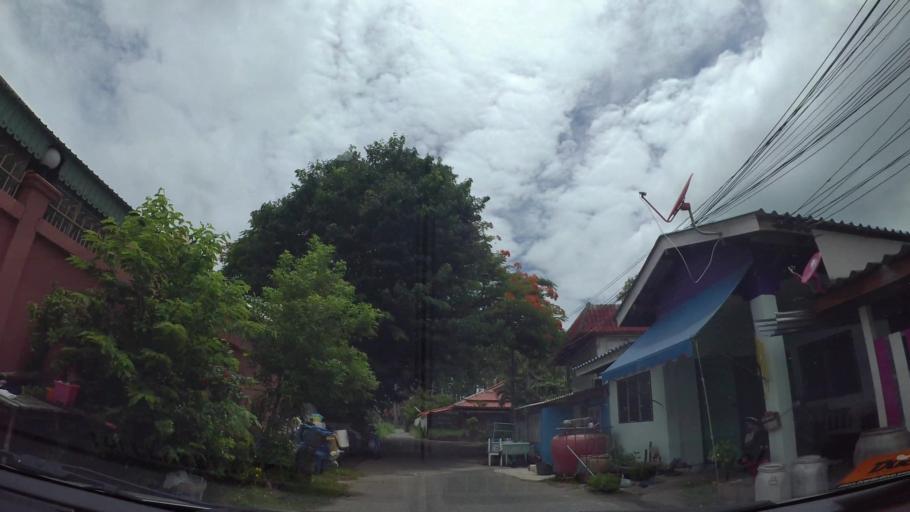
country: TH
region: Chon Buri
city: Sattahip
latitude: 12.7647
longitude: 100.8948
